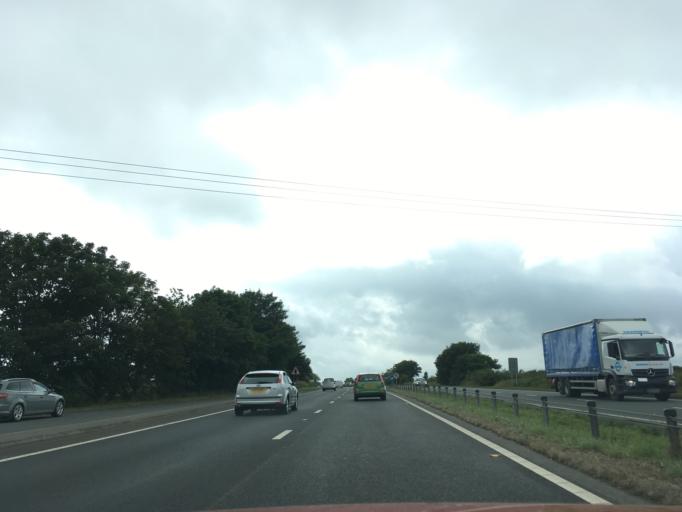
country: GB
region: Wales
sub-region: Carmarthenshire
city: Saint Clears
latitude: 51.8267
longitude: -4.4644
